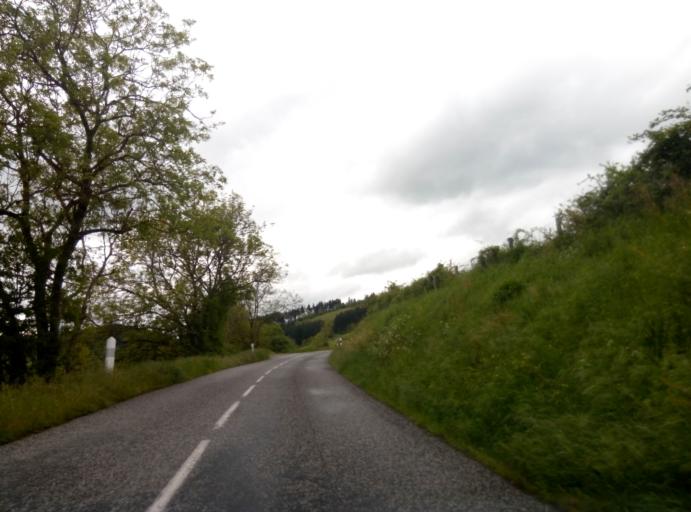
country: FR
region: Rhone-Alpes
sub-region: Departement du Rhone
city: Tarare
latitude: 45.9149
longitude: 4.4284
